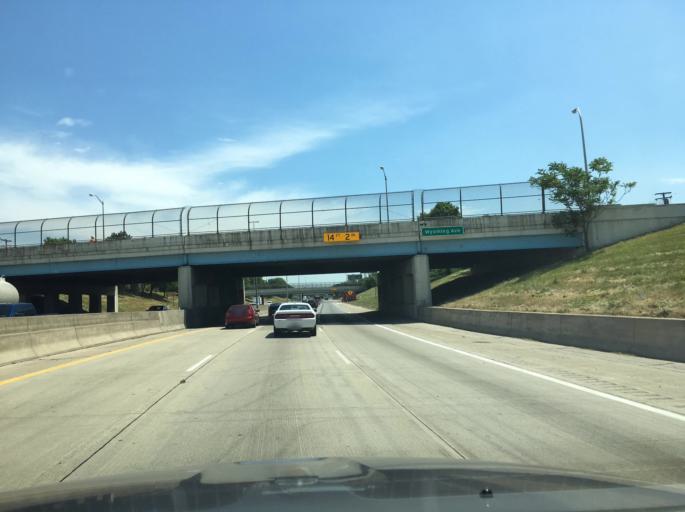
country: US
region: Michigan
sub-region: Wayne County
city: Dearborn
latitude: 42.3286
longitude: -83.1573
